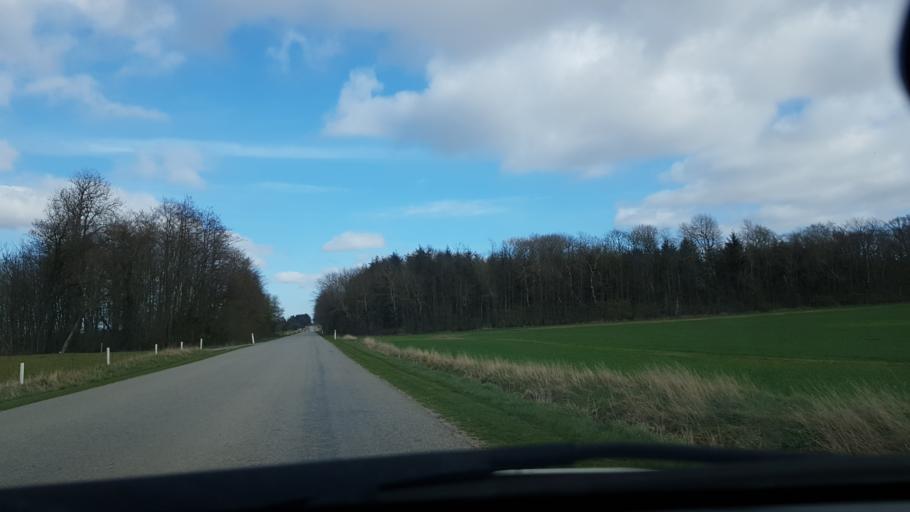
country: DK
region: South Denmark
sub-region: Vejen Kommune
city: Rodding
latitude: 55.4262
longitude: 9.0696
